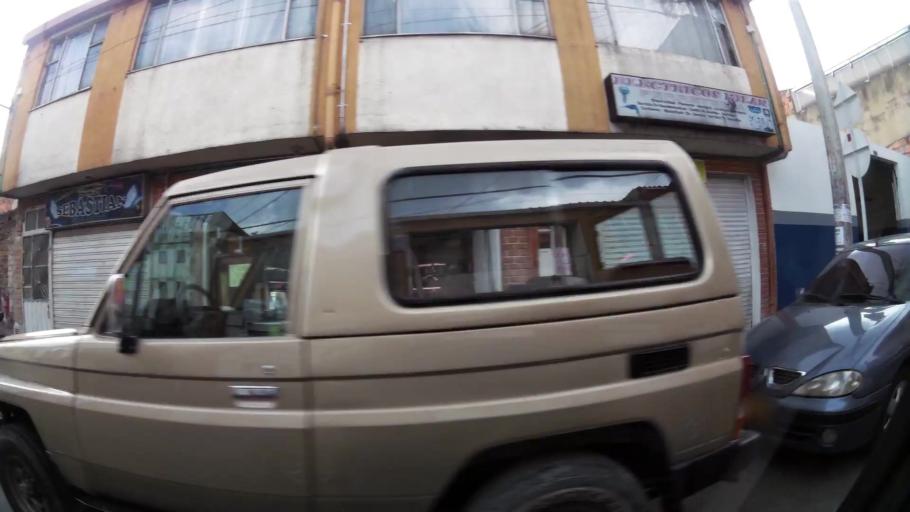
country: CO
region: Cundinamarca
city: La Calera
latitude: 4.7389
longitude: -74.0266
